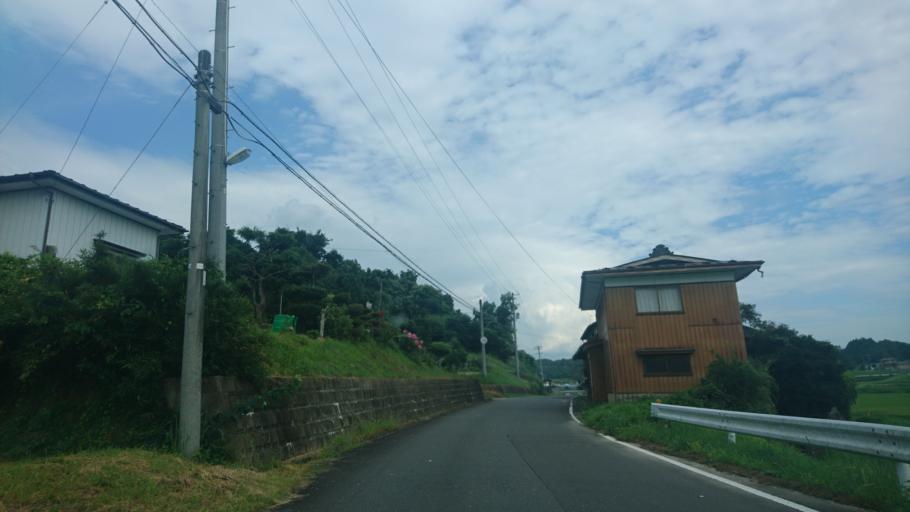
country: JP
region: Miyagi
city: Furukawa
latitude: 38.7637
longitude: 140.9808
